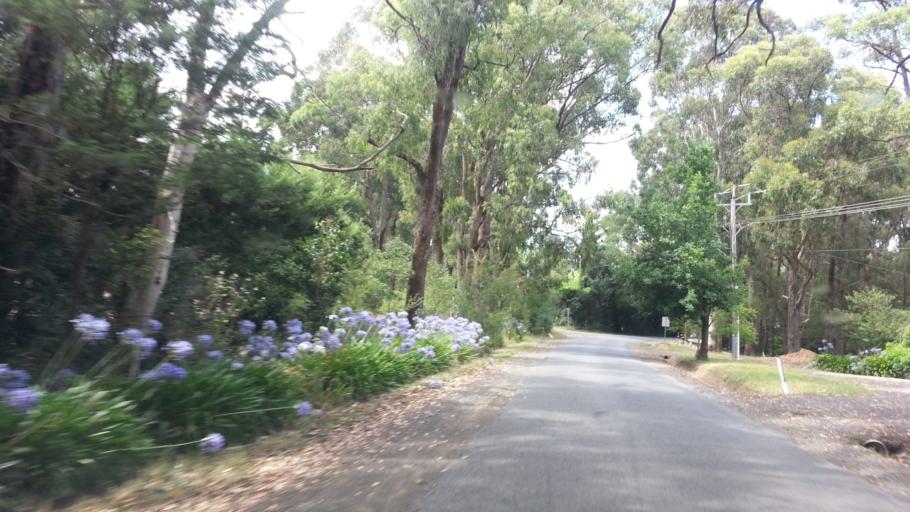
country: AU
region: Victoria
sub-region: Cardinia
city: Emerald
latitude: -37.9416
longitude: 145.4407
